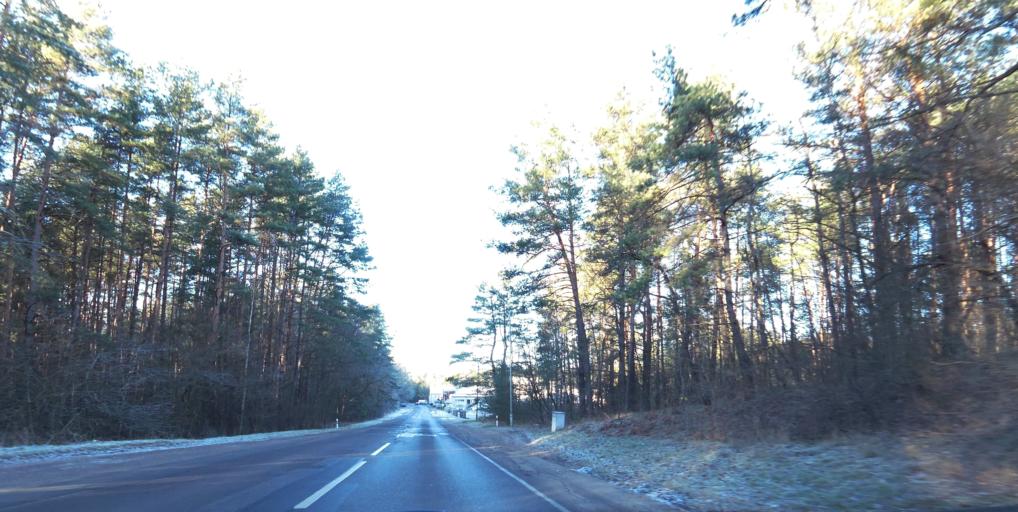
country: LT
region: Vilnius County
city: Lazdynai
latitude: 54.6398
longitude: 25.1783
